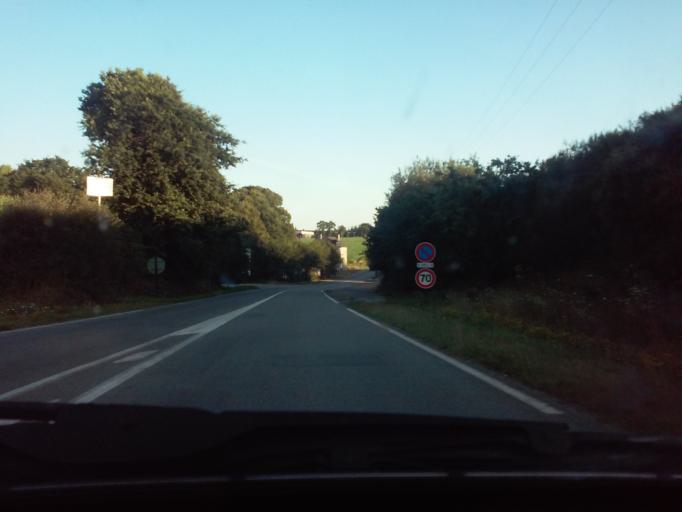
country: FR
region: Brittany
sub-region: Departement des Cotes-d'Armor
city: Saint-Samson-sur-Rance
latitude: 48.4801
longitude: -2.0419
